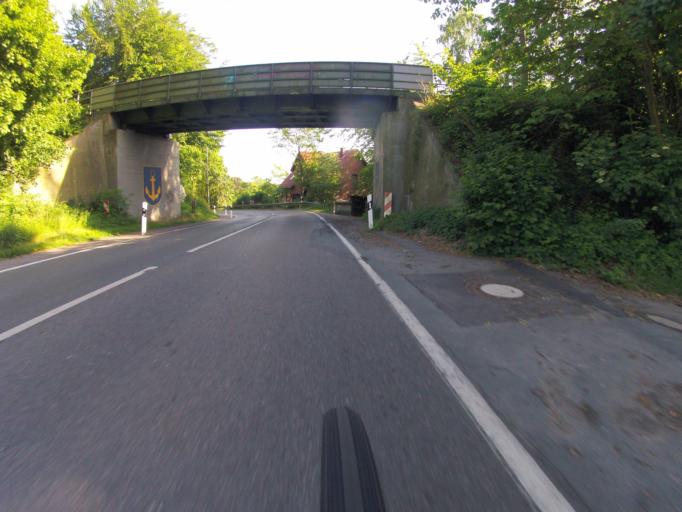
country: DE
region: North Rhine-Westphalia
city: Ibbenburen
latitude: 52.2927
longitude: 7.6977
